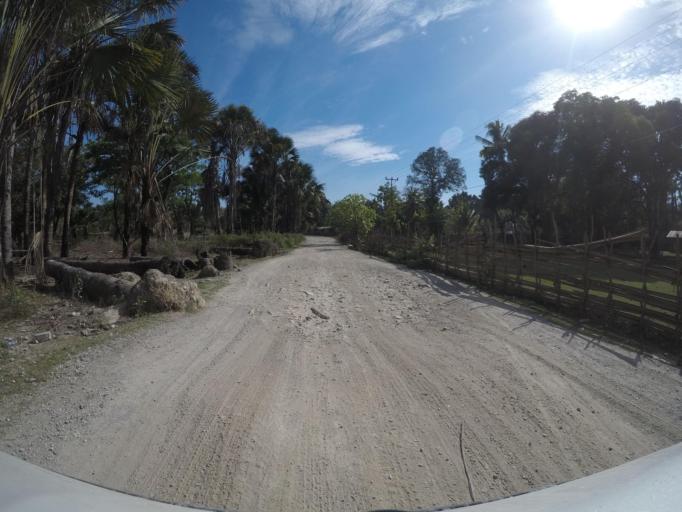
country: TL
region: Bobonaro
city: Maliana
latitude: -8.8753
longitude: 125.2121
